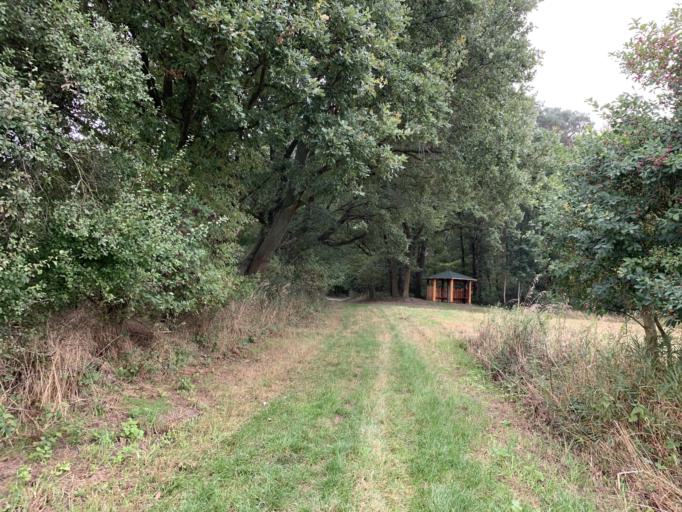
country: DE
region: Mecklenburg-Vorpommern
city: Blankensee
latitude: 53.3935
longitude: 13.2554
